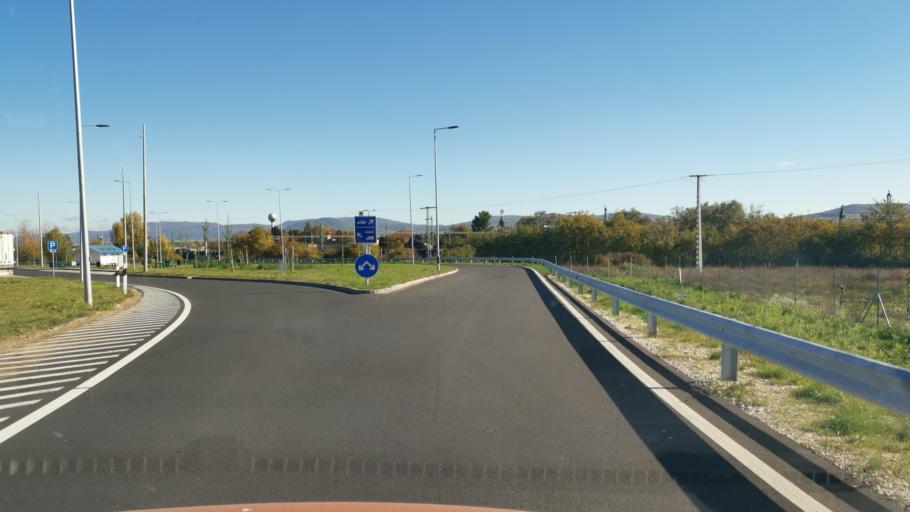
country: HU
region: Borsod-Abauj-Zemplen
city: Gonc
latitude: 48.5073
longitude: 21.2263
